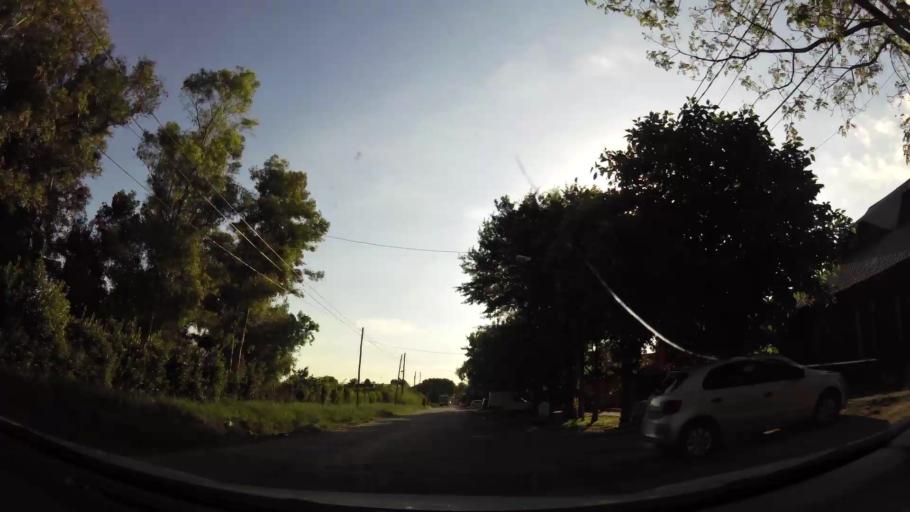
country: AR
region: Buenos Aires
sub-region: Partido de Tigre
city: Tigre
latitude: -34.4661
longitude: -58.6561
